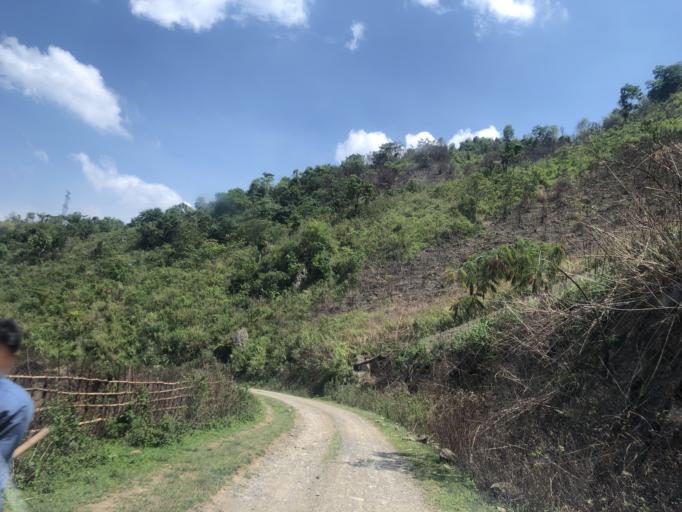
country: LA
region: Phongsali
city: Phongsali
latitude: 21.3972
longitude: 102.2160
